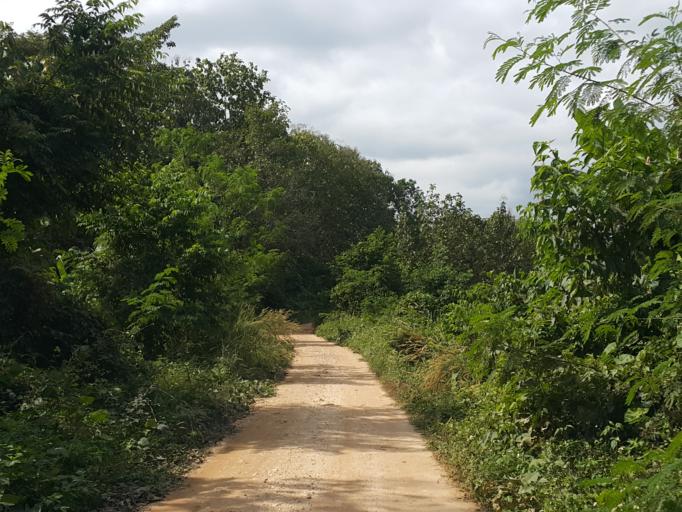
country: TH
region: Lampang
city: Hang Chat
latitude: 18.4885
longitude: 99.4061
